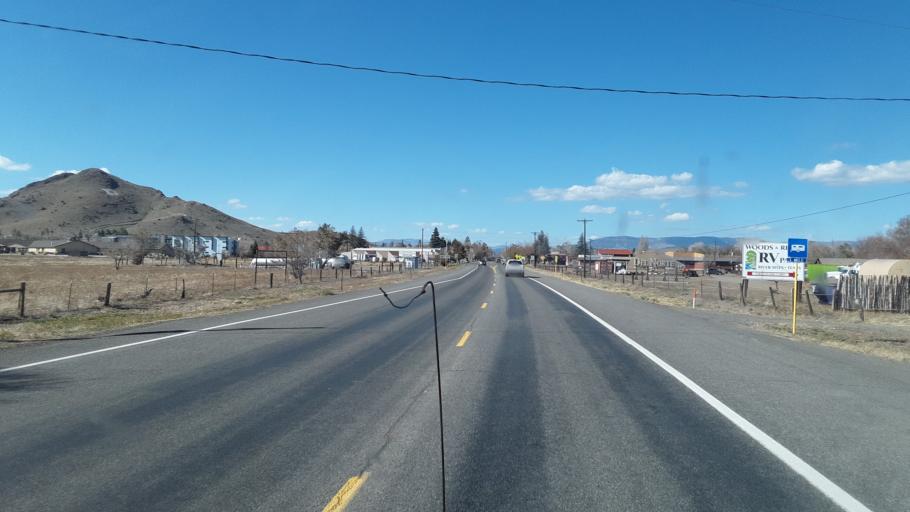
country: US
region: Colorado
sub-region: Rio Grande County
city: Del Norte
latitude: 37.6779
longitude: -106.3412
